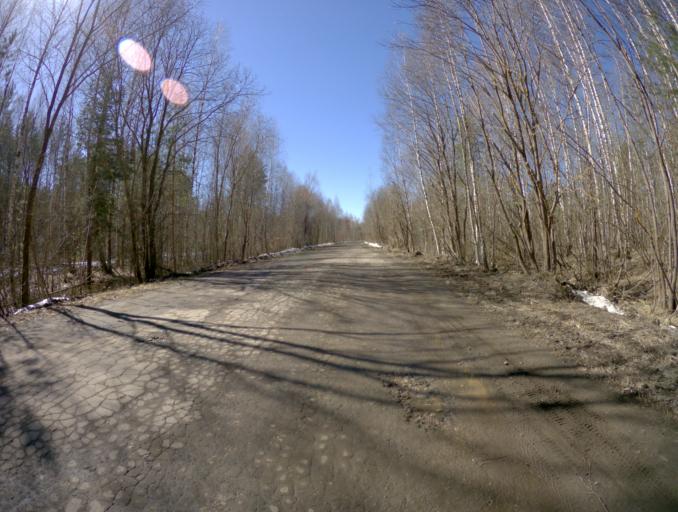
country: RU
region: Vladimir
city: Orgtrud
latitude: 56.2814
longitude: 40.7203
